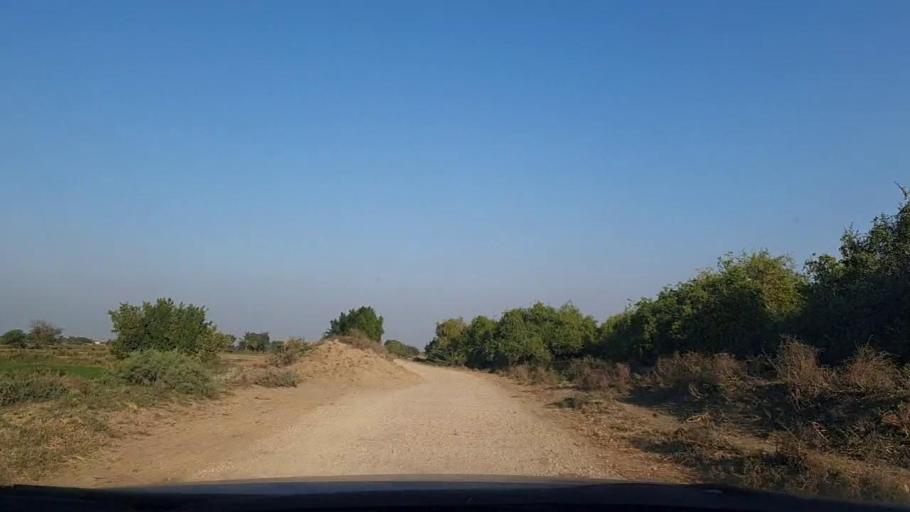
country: PK
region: Sindh
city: Mirpur Sakro
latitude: 24.5217
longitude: 67.6447
